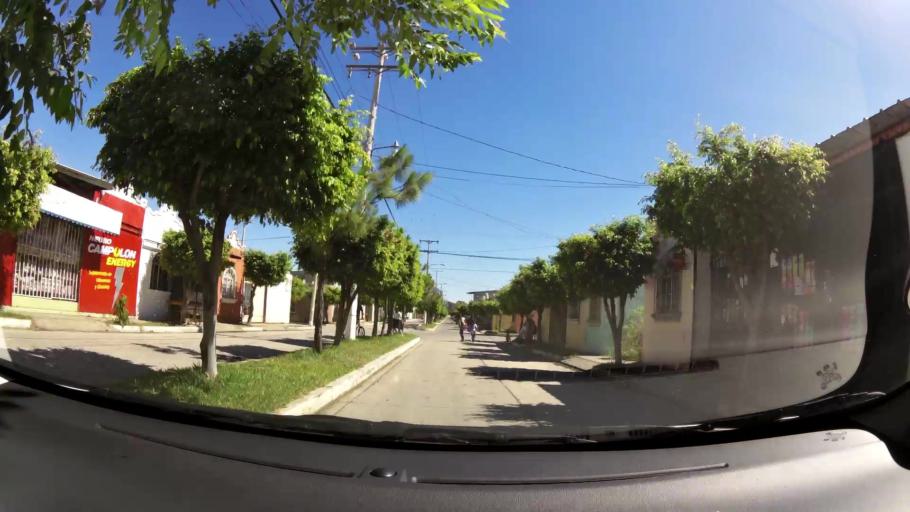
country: SV
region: La Libertad
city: San Juan Opico
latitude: 13.7964
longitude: -89.3575
